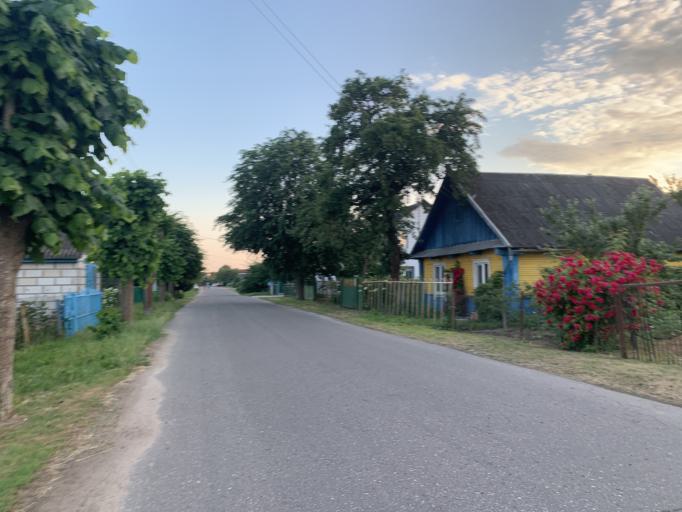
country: BY
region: Minsk
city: Nyasvizh
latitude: 53.2168
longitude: 26.6731
